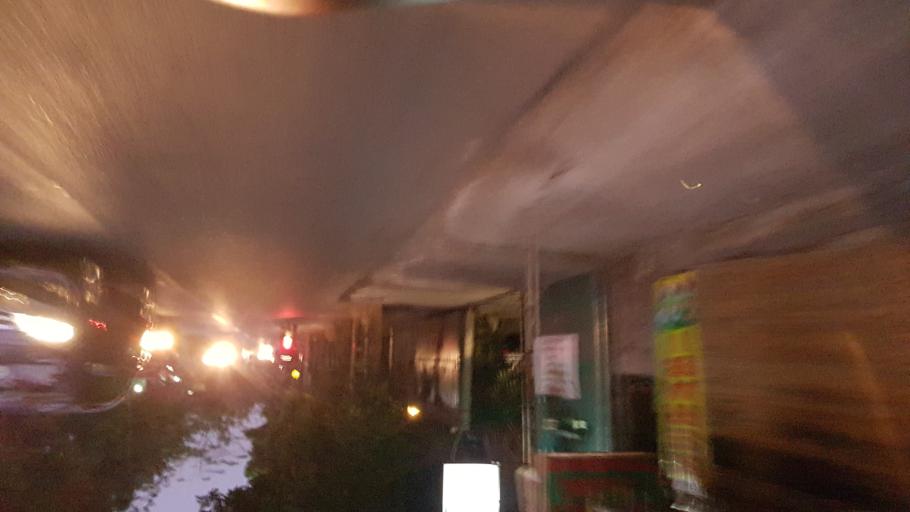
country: ID
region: Jakarta Raya
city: Jakarta
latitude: -6.2989
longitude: 106.8263
